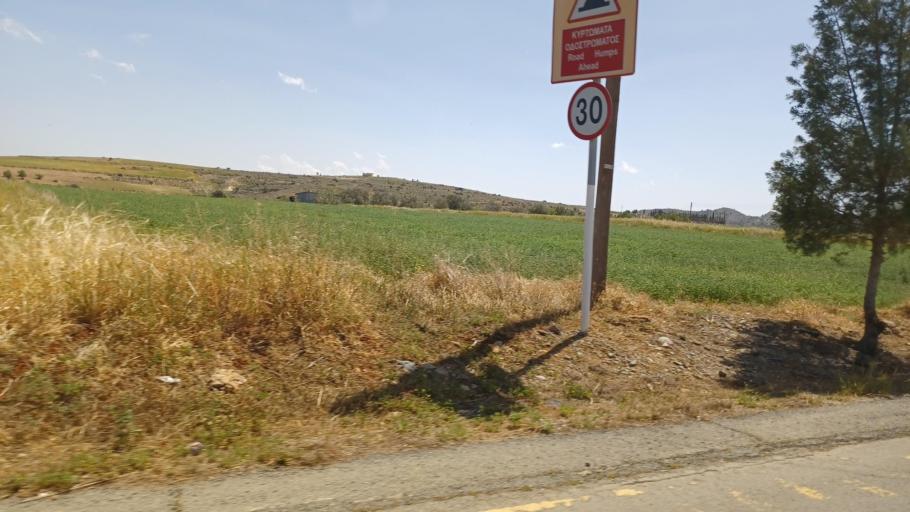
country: CY
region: Lefkosia
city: Astromeritis
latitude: 35.0827
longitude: 33.0159
